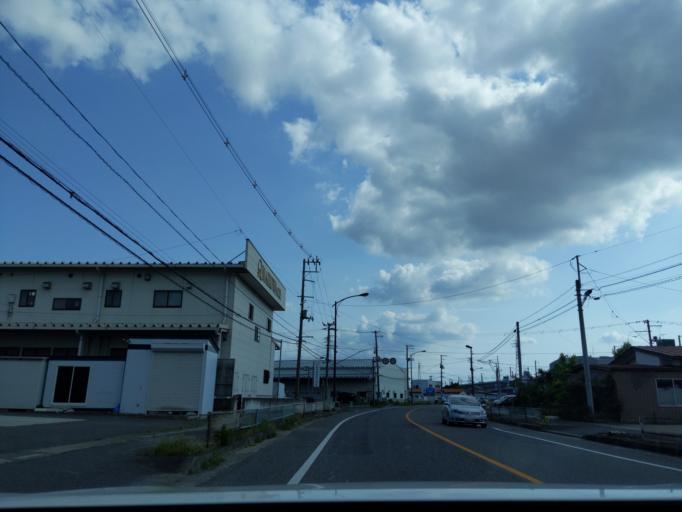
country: JP
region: Fukushima
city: Koriyama
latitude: 37.3690
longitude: 140.3809
